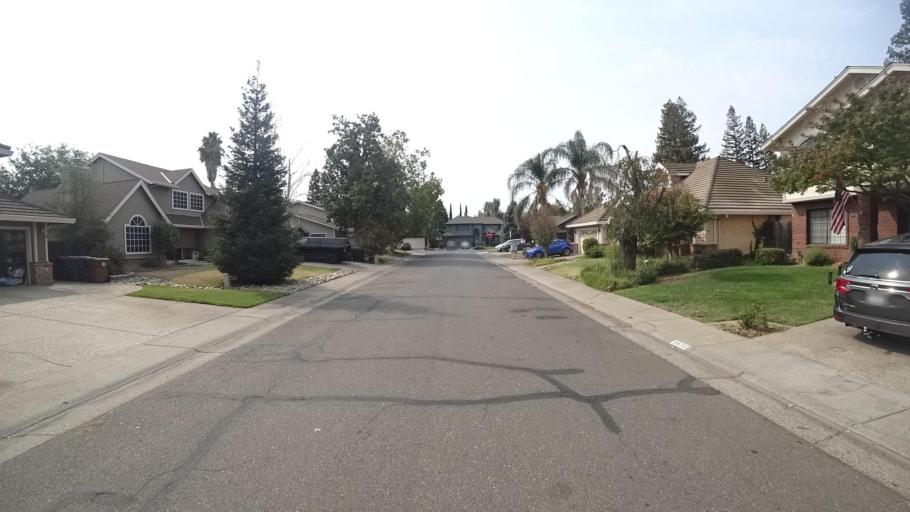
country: US
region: California
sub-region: Sacramento County
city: Elk Grove
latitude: 38.4033
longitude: -121.3750
